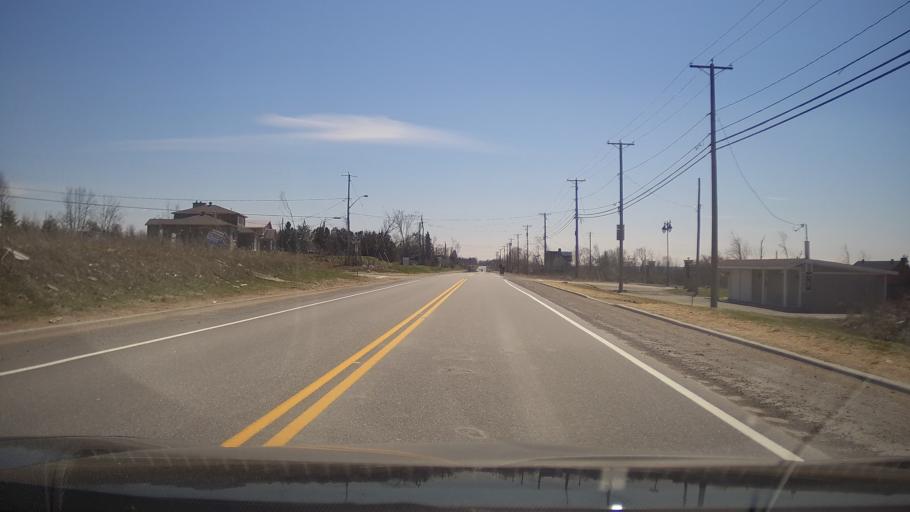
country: CA
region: Ontario
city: Bells Corners
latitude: 45.4366
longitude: -75.9101
